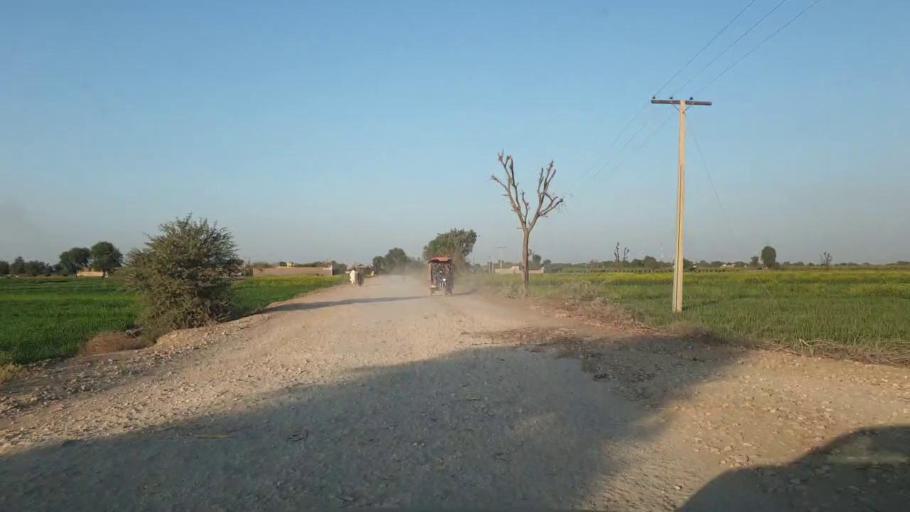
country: PK
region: Sindh
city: Tando Allahyar
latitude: 25.3848
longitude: 68.7548
